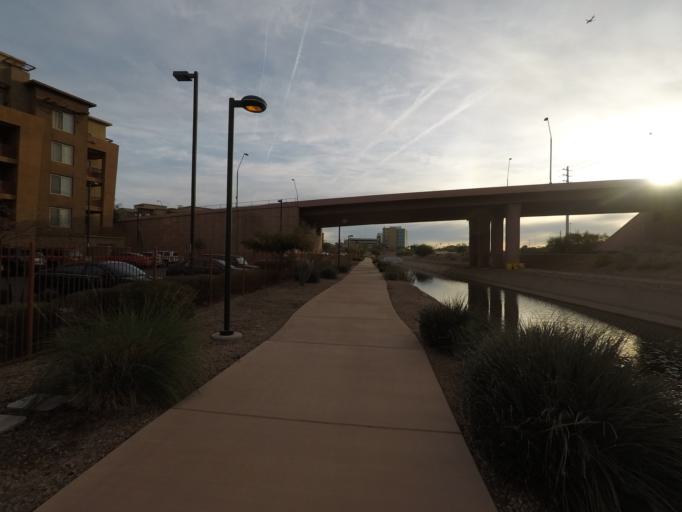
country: US
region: Arizona
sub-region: Maricopa County
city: Tempe Junction
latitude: 33.4377
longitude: -111.9501
